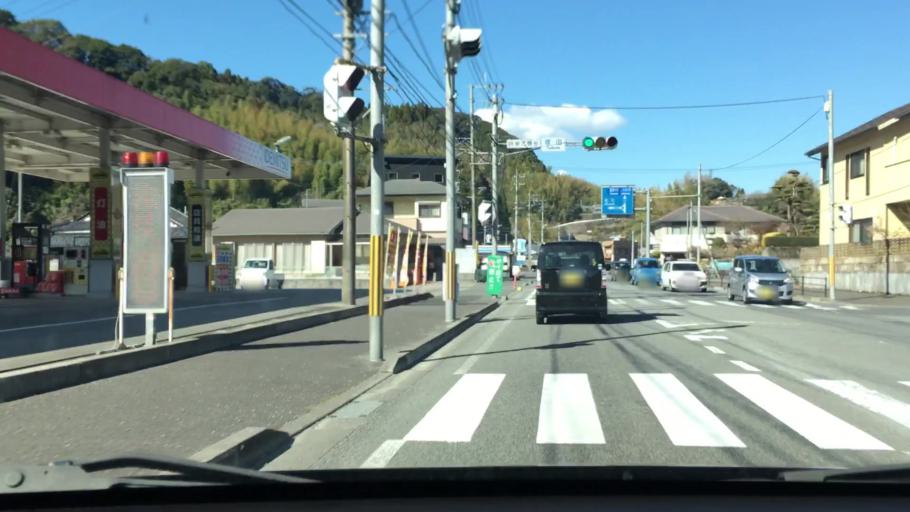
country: JP
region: Kagoshima
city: Ijuin
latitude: 31.6547
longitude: 130.4972
